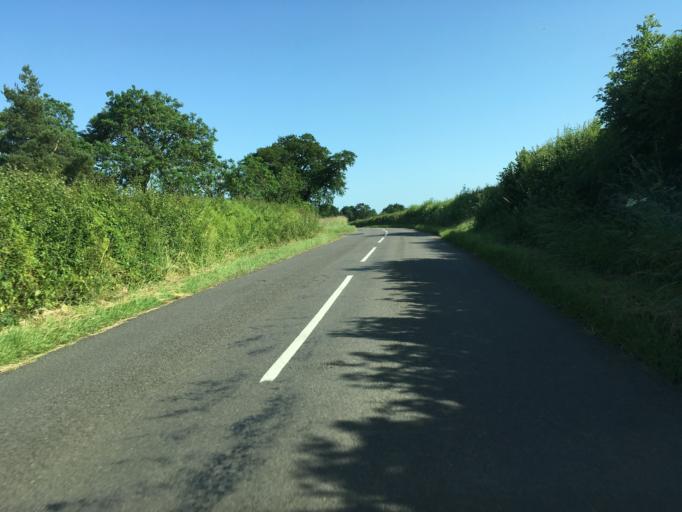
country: GB
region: England
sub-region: Buckinghamshire
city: Steeple Claydon
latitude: 51.9417
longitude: -0.9454
